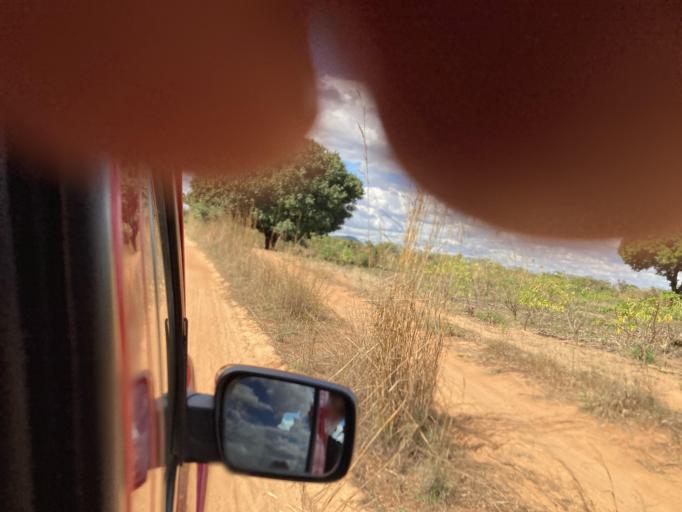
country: MZ
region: Cabo Delgado
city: Montepuez
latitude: -13.1254
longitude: 39.0468
